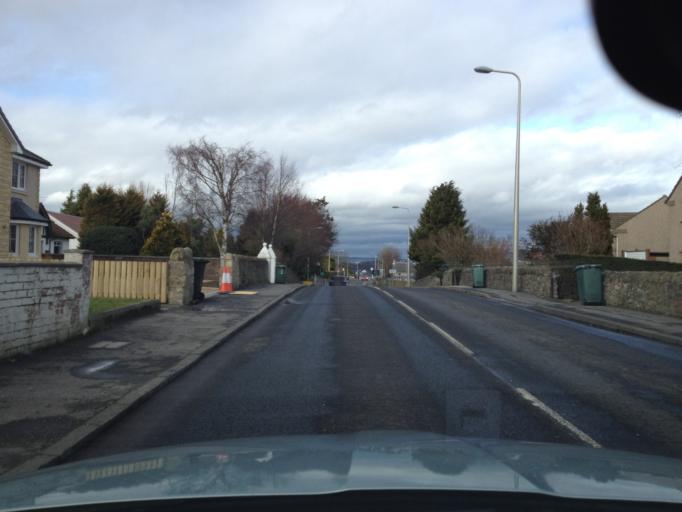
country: GB
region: Scotland
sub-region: Edinburgh
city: Queensferry
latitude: 55.9851
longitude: -3.3965
